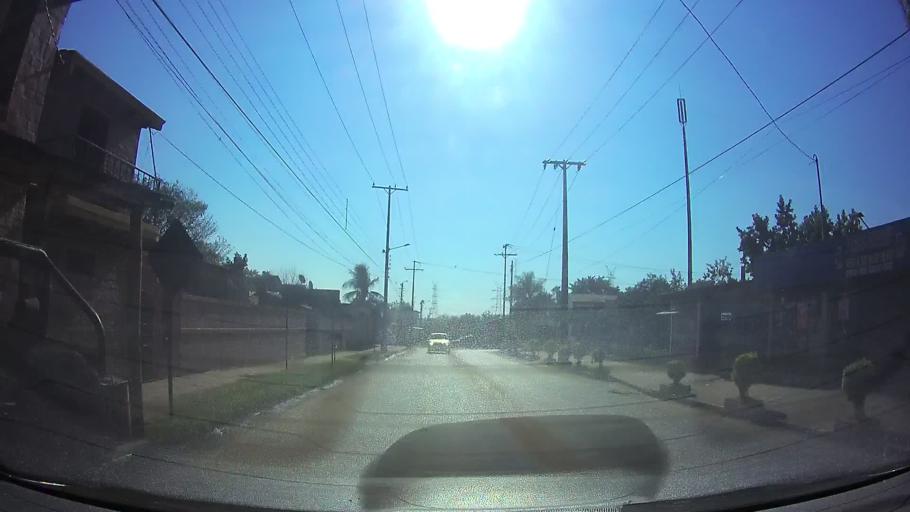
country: PY
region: Asuncion
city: Asuncion
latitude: -25.2503
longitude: -57.5858
